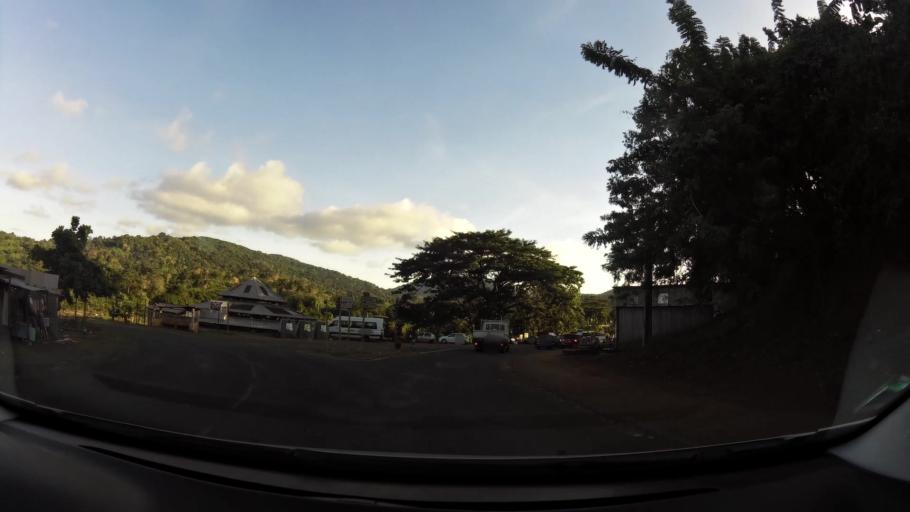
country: YT
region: Dembeni
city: Dembeni
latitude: -12.8365
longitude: 45.1773
